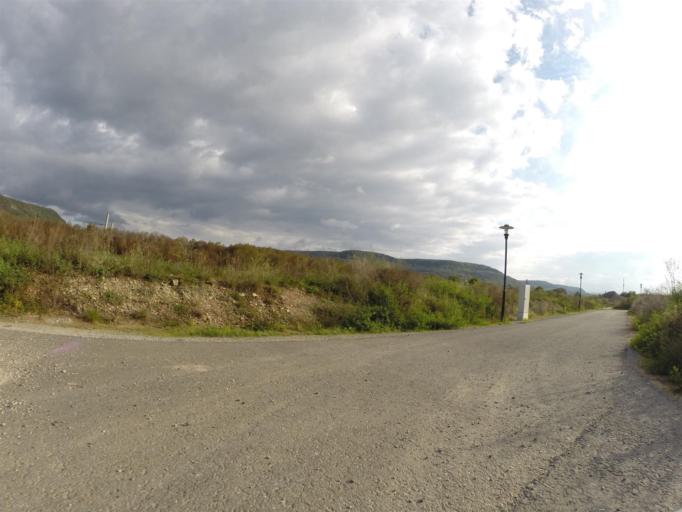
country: DE
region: Thuringia
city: Neuengonna
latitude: 50.9601
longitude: 11.6239
